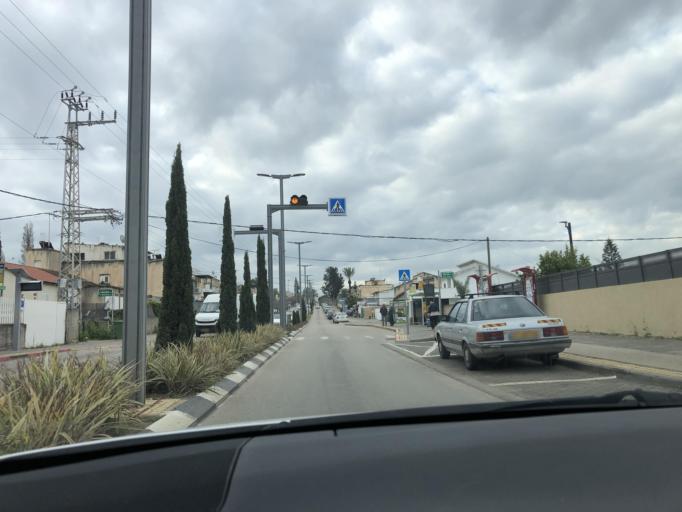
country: IL
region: Central District
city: Rosh Ha'Ayin
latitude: 32.0958
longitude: 34.9545
